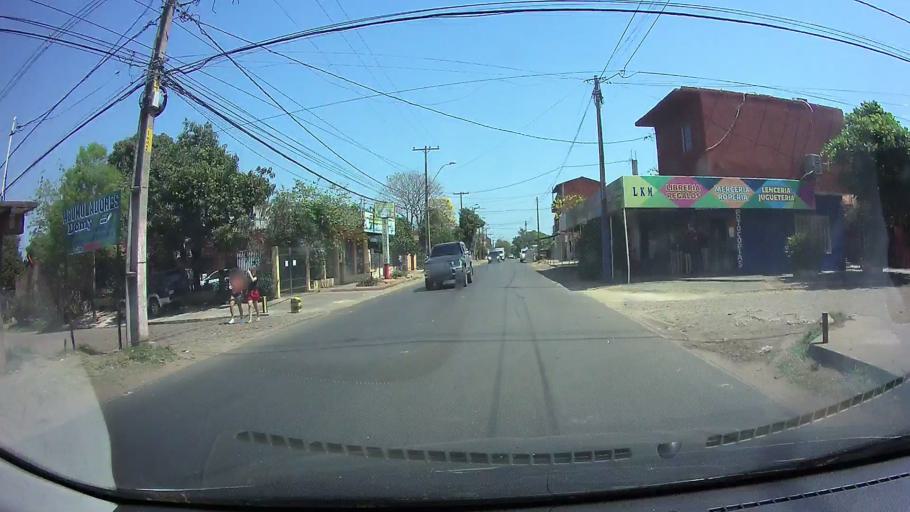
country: PY
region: Central
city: Colonia Mariano Roque Alonso
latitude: -25.2063
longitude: -57.5185
